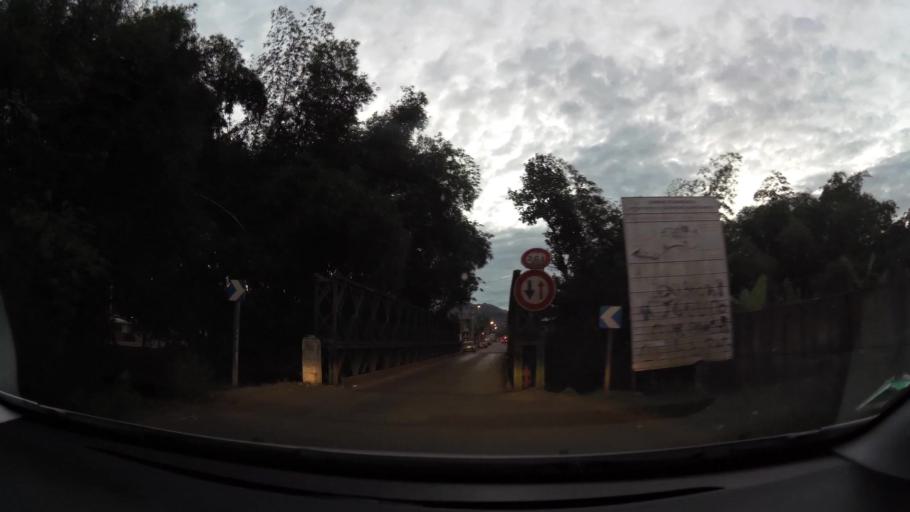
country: YT
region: Bandraboua
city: Bandraboua
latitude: -12.7232
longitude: 45.1216
